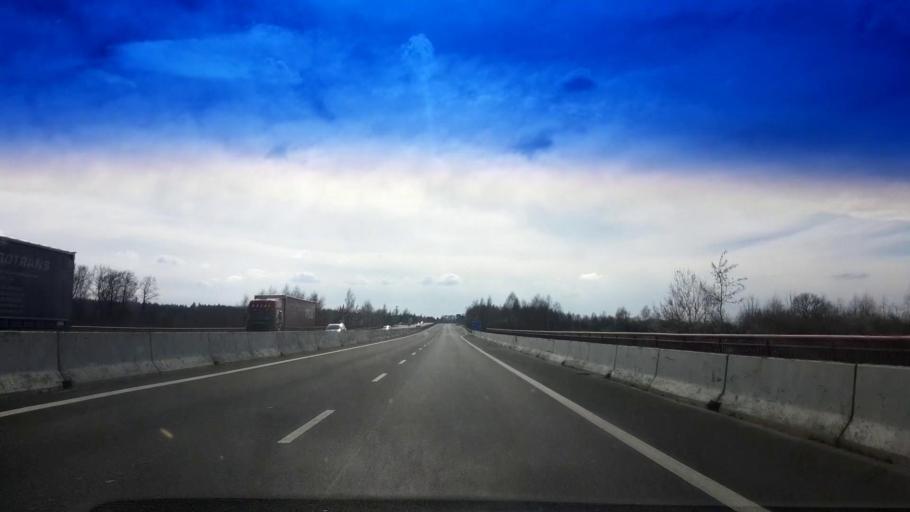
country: DE
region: Bavaria
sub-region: Upper Franconia
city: Schirnding
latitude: 50.0916
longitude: 12.2749
